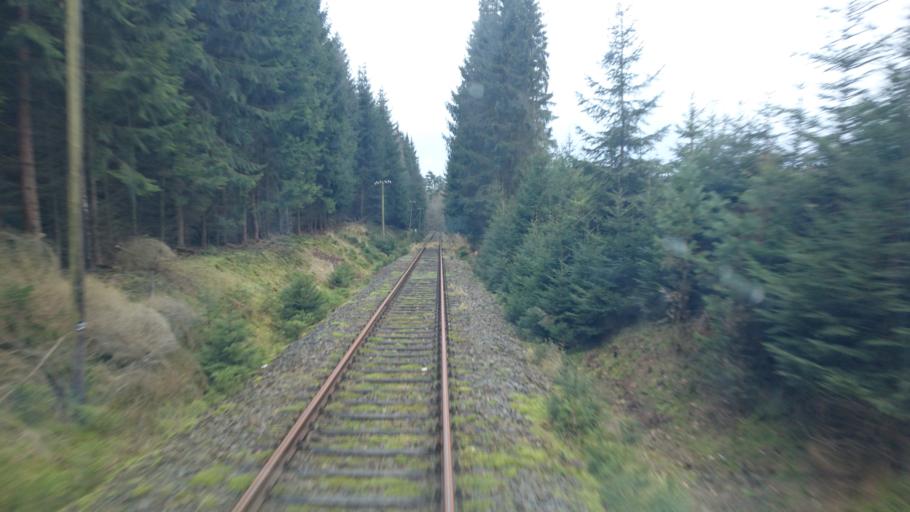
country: DE
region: Thuringia
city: Kirschkau
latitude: 50.5706
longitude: 11.8914
